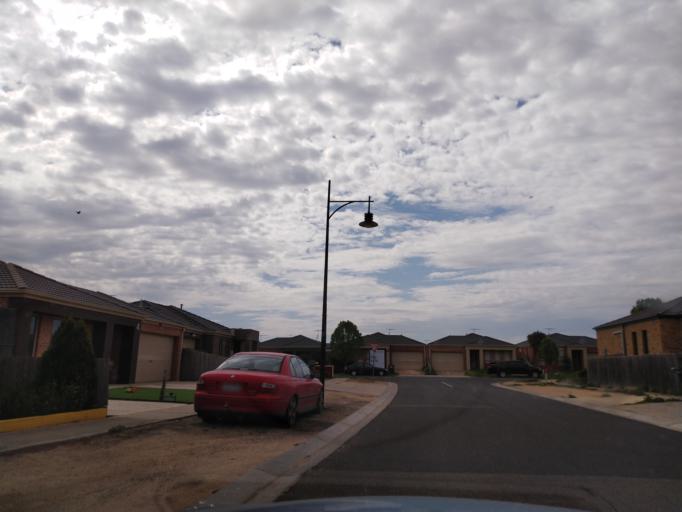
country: AU
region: Victoria
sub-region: Wyndham
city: Williams Landing
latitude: -37.8450
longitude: 144.7167
